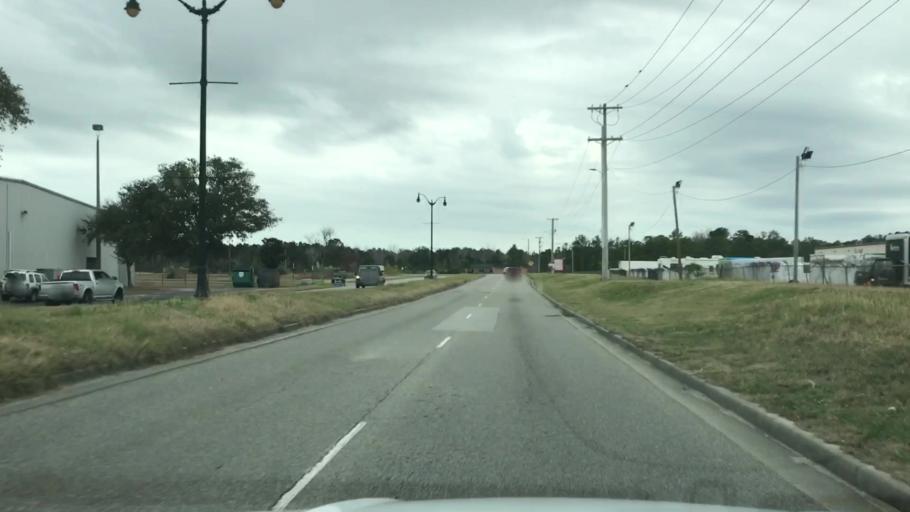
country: US
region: South Carolina
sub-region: Horry County
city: Forestbrook
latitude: 33.7122
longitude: -78.9389
